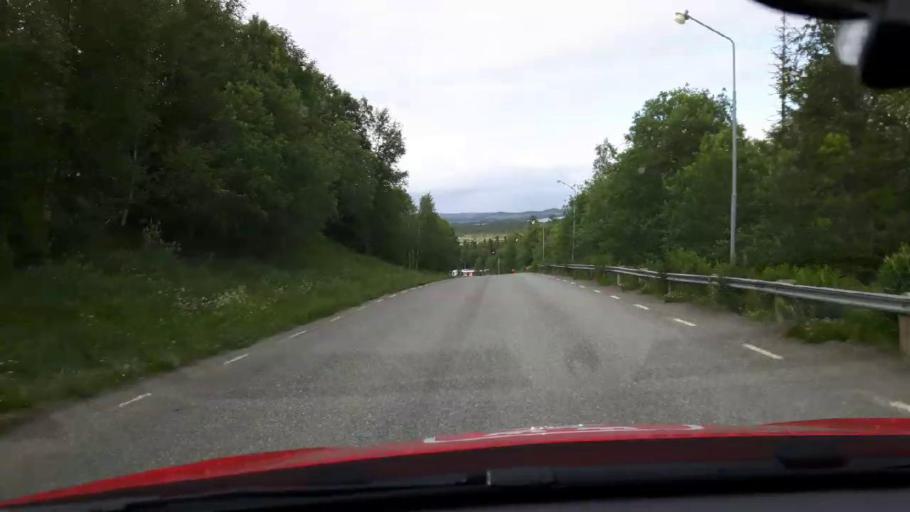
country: SE
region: Jaemtland
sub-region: Are Kommun
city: Are
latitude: 63.2529
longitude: 12.4527
